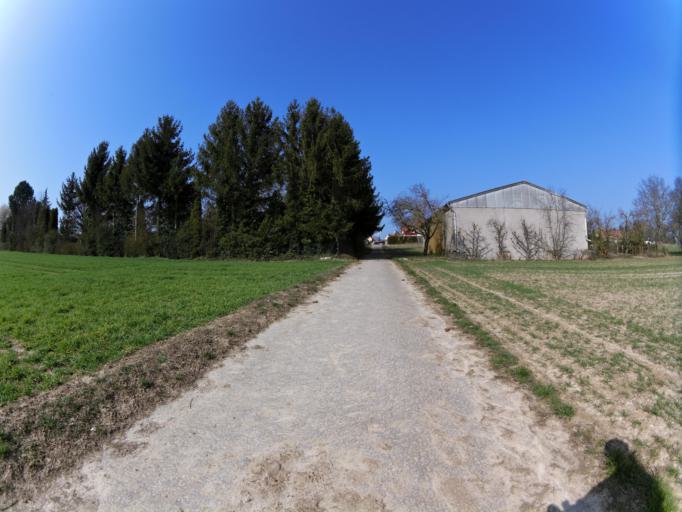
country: DE
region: Bavaria
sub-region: Regierungsbezirk Unterfranken
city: Geroldshausen
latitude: 49.6825
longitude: 9.9072
